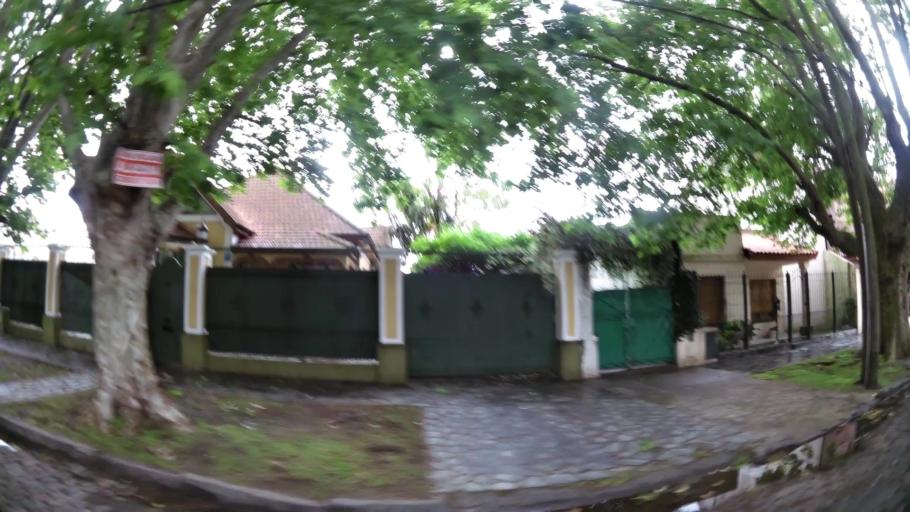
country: AR
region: Buenos Aires
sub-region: Partido de Lomas de Zamora
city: Lomas de Zamora
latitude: -34.7492
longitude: -58.3912
